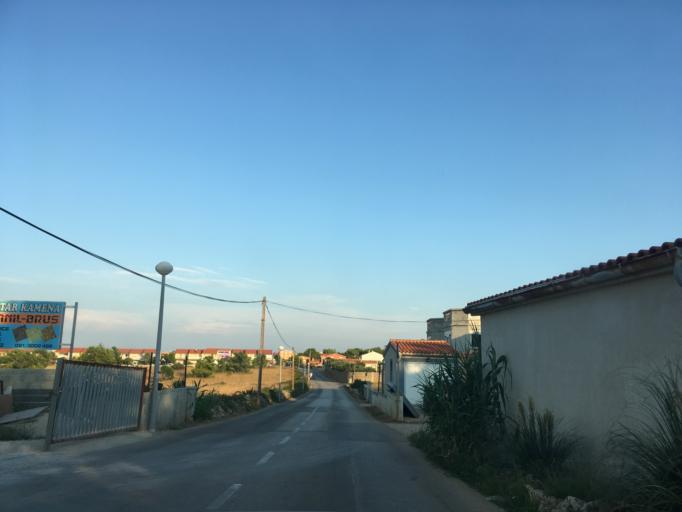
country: HR
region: Zadarska
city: Vir
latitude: 44.3022
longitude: 15.1080
